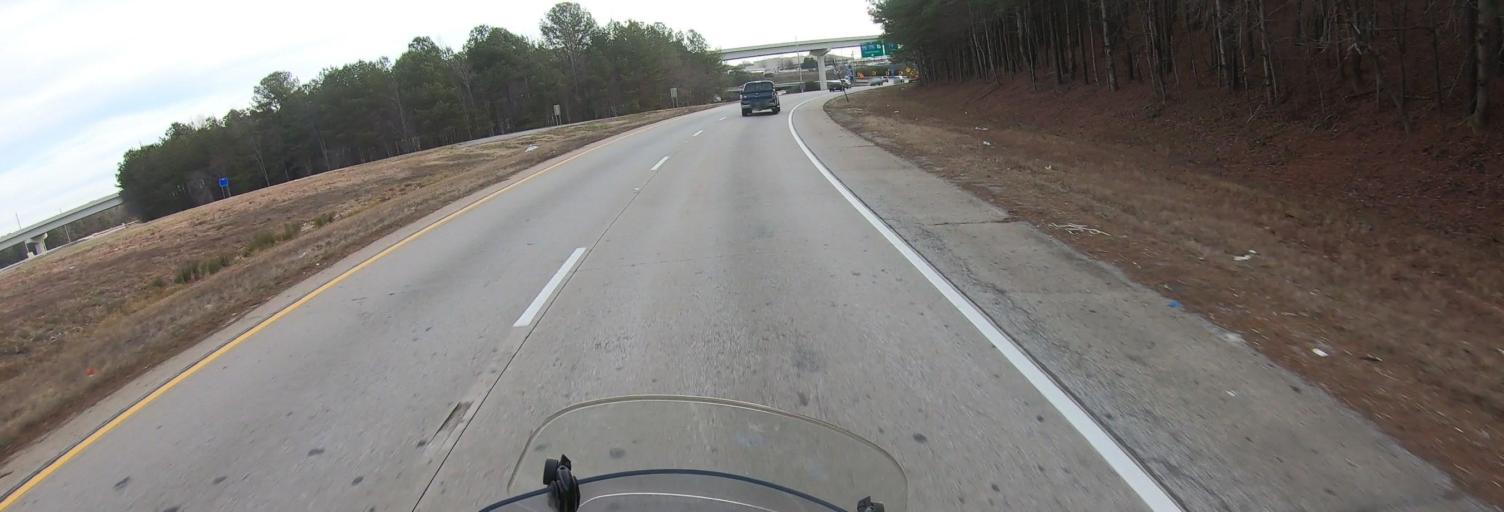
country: US
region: Georgia
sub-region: Cobb County
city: Marietta
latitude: 33.9776
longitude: -84.5453
